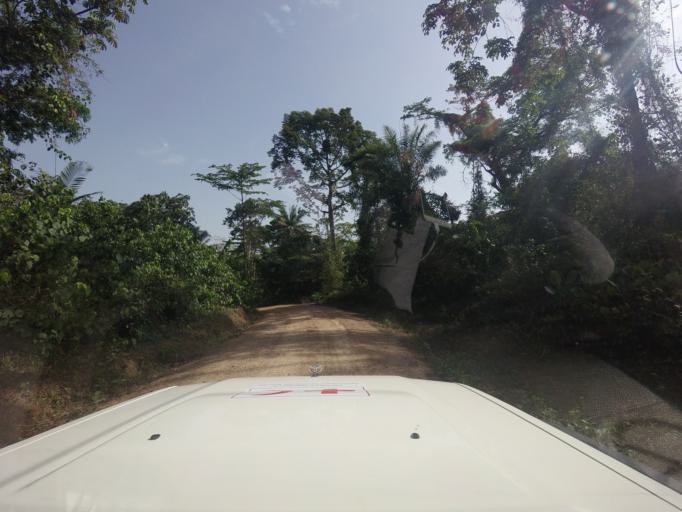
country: LR
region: Lofa
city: Voinjama
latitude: 8.5130
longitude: -9.7627
